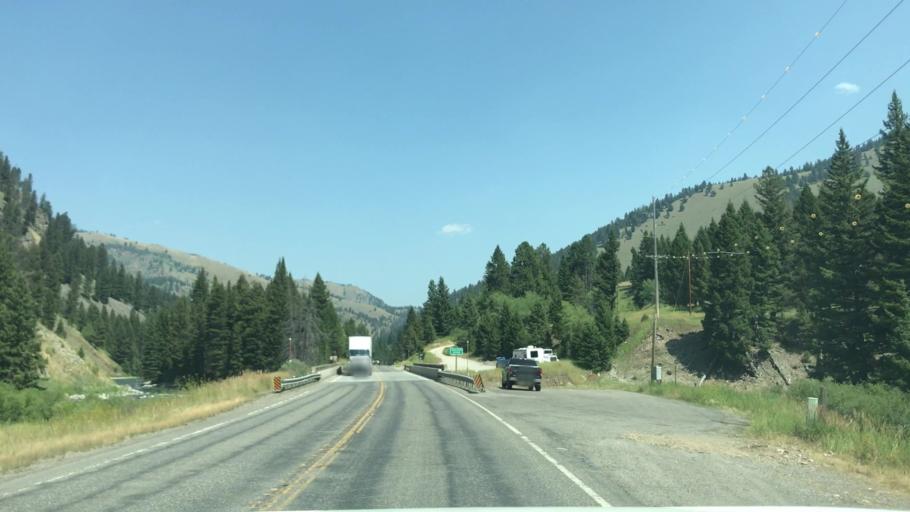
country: US
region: Montana
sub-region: Gallatin County
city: Big Sky
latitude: 45.2811
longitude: -111.2263
